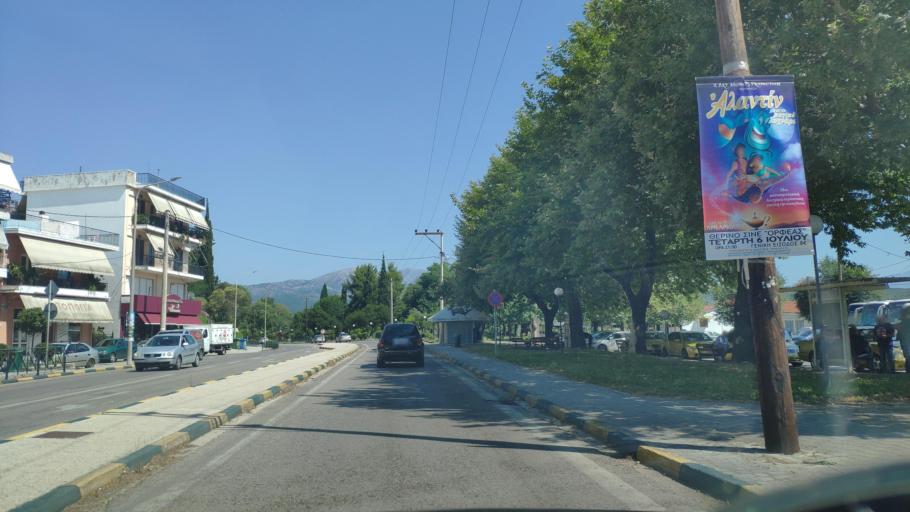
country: GR
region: Epirus
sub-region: Nomos Artas
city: Arta
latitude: 39.1593
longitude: 20.9954
